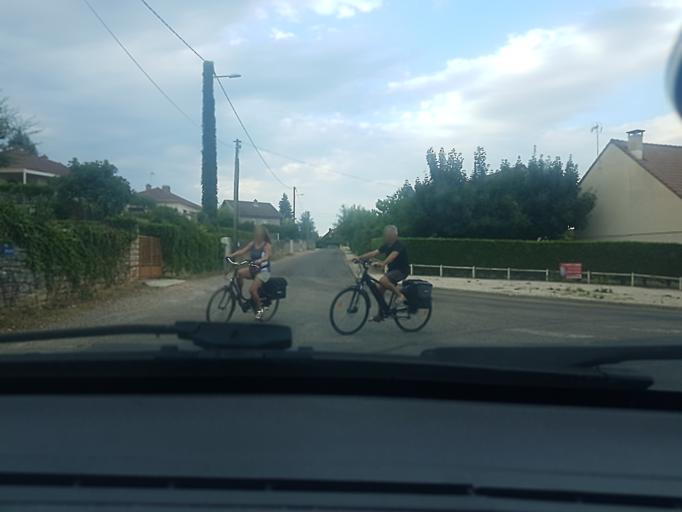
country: FR
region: Bourgogne
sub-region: Departement de Saone-et-Loire
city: Givry
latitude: 46.7776
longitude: 4.7436
